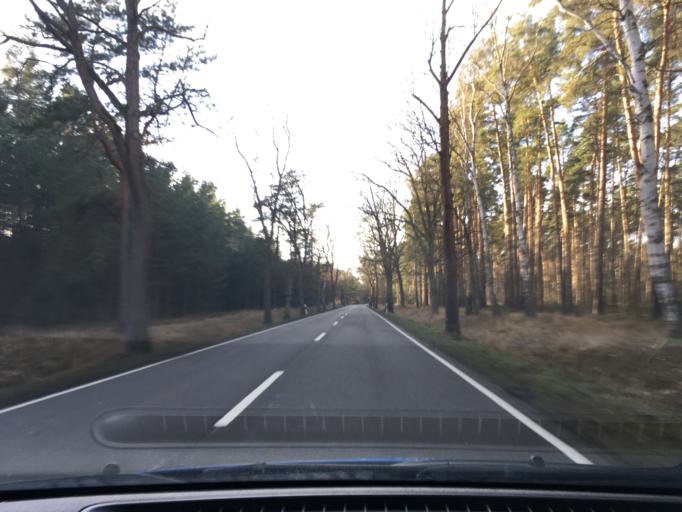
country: DE
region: Saxony-Anhalt
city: Seehausen
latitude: 52.8831
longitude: 11.6203
